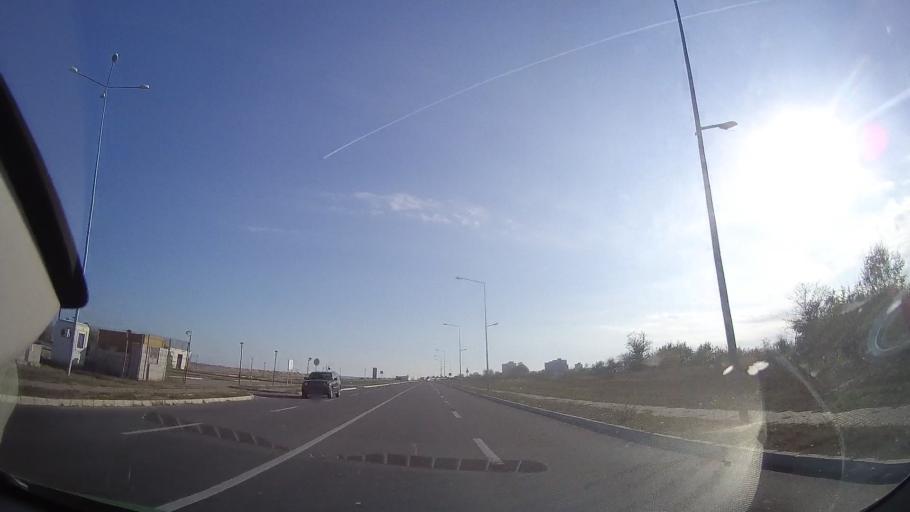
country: RO
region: Constanta
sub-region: Municipiul Mangalia
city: Mangalia
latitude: 43.8426
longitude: 28.5894
